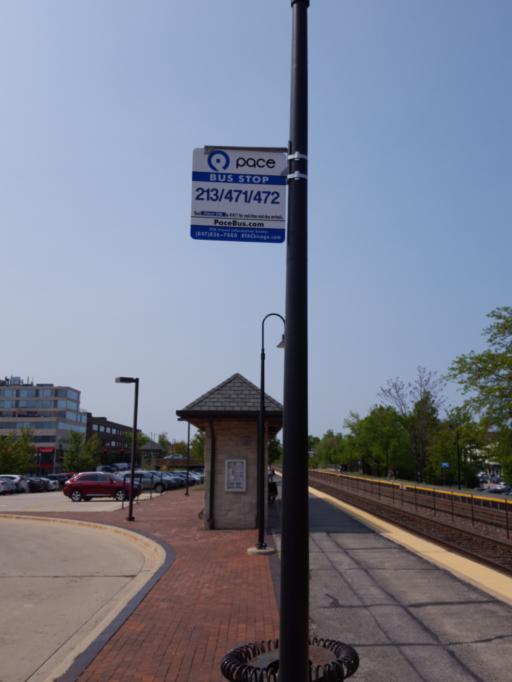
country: US
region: Illinois
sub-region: Lake County
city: Highland Park
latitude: 42.1833
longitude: -87.7977
